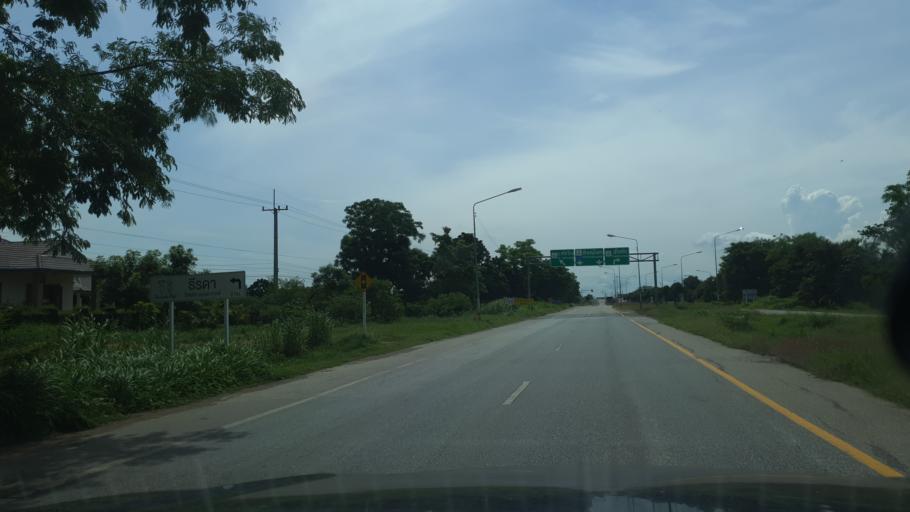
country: TH
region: Sukhothai
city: Sukhothai
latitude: 17.0730
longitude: 99.8279
